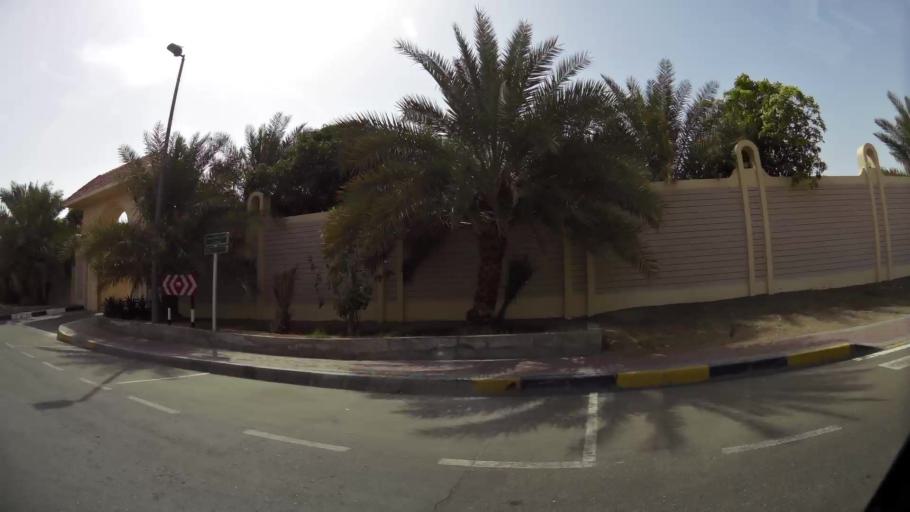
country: AE
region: Abu Dhabi
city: Al Ain
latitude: 24.1672
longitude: 55.7006
